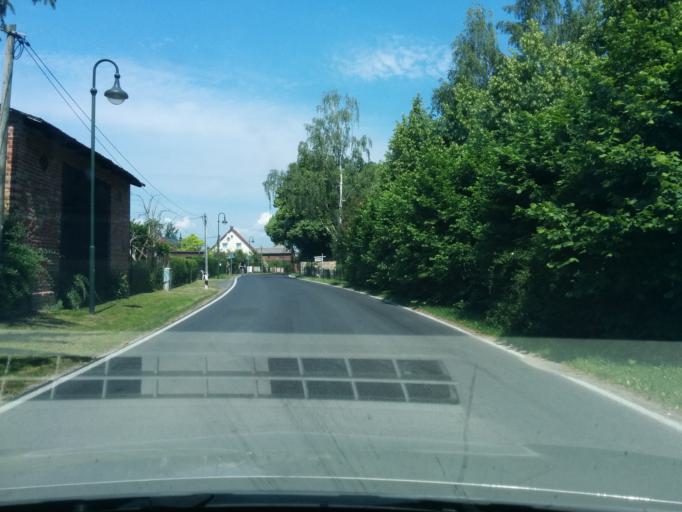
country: DE
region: Brandenburg
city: Ahrensfelde
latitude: 52.6268
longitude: 13.5745
